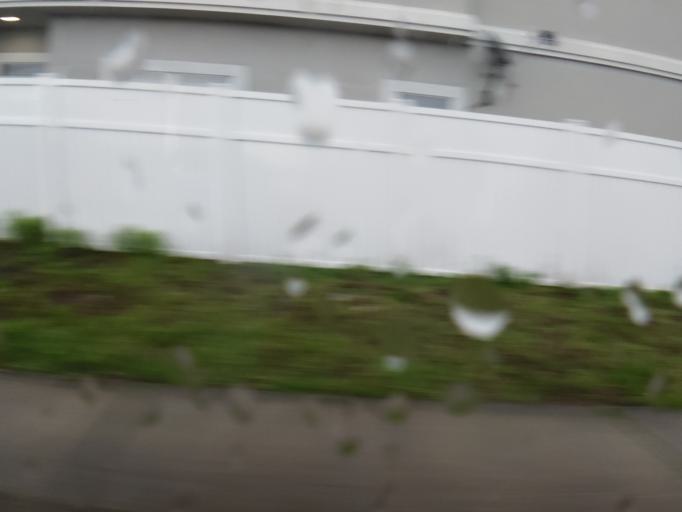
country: US
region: Florida
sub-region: Duval County
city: Jacksonville Beach
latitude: 30.2780
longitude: -81.3965
